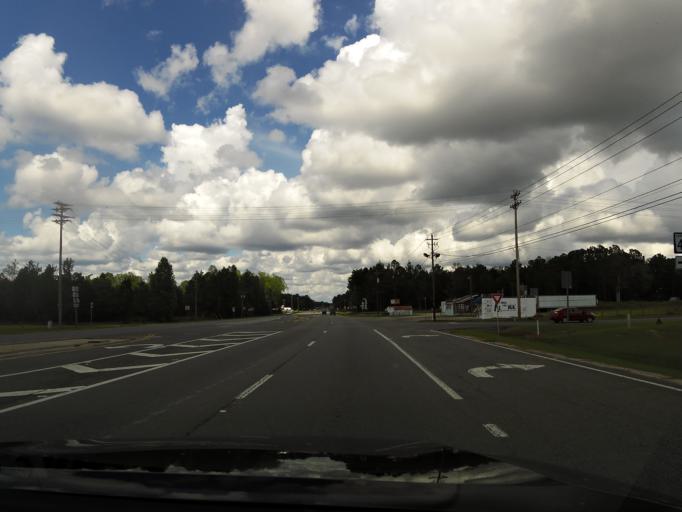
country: US
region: Georgia
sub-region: Charlton County
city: Folkston
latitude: 30.8432
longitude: -82.0066
